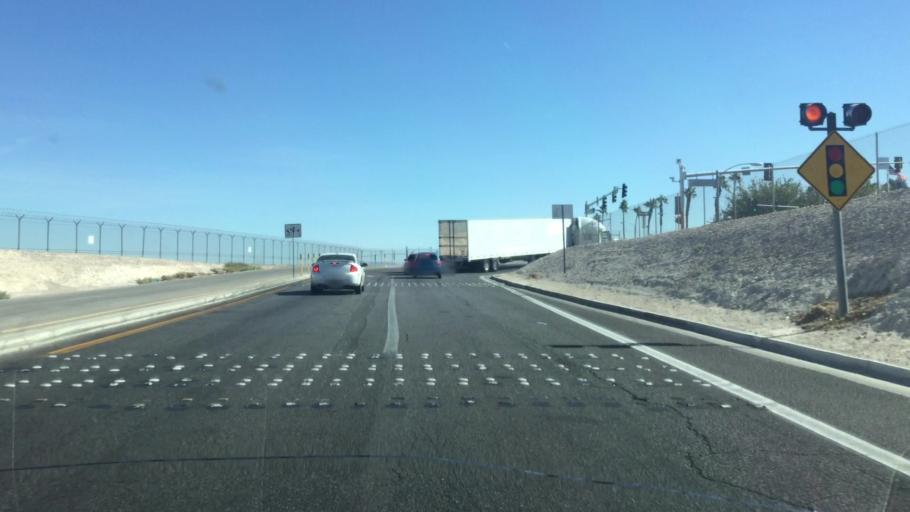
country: US
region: Nevada
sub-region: Clark County
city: Paradise
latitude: 36.0720
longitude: -115.1421
